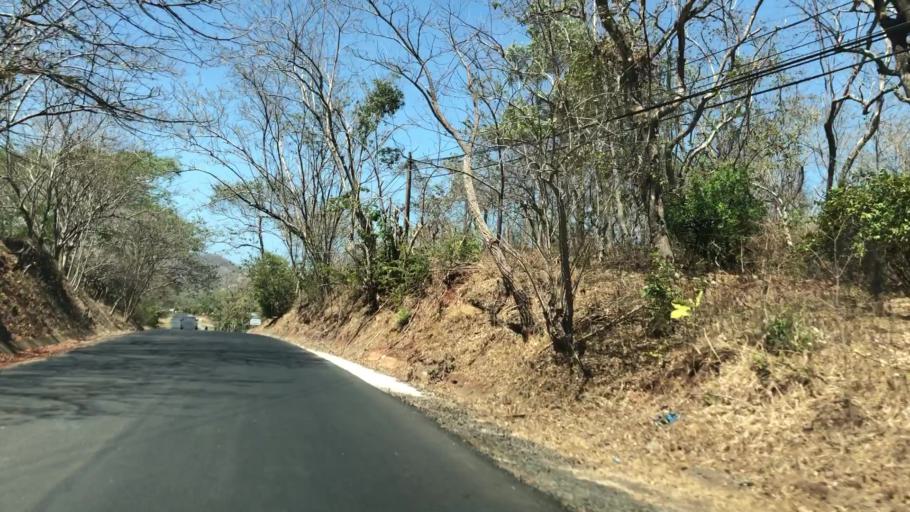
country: CR
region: Guanacaste
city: Sardinal
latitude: 10.3660
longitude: -85.7998
